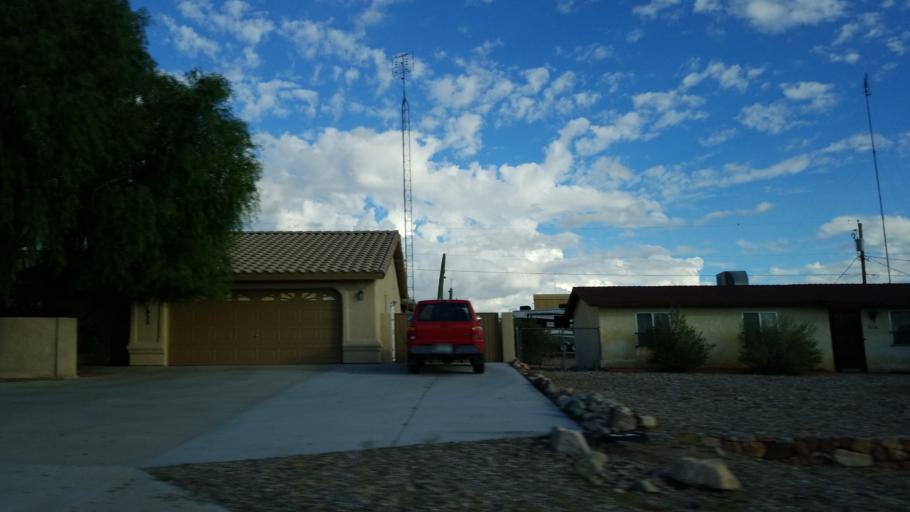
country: US
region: Arizona
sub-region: Mohave County
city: Lake Havasu City
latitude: 34.4572
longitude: -114.2596
